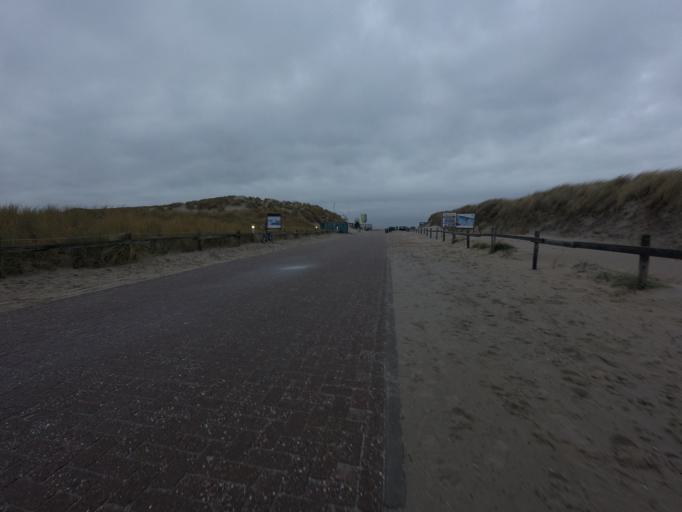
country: NL
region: North Holland
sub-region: Gemeente Texel
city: Den Burg
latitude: 53.0808
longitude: 4.7382
